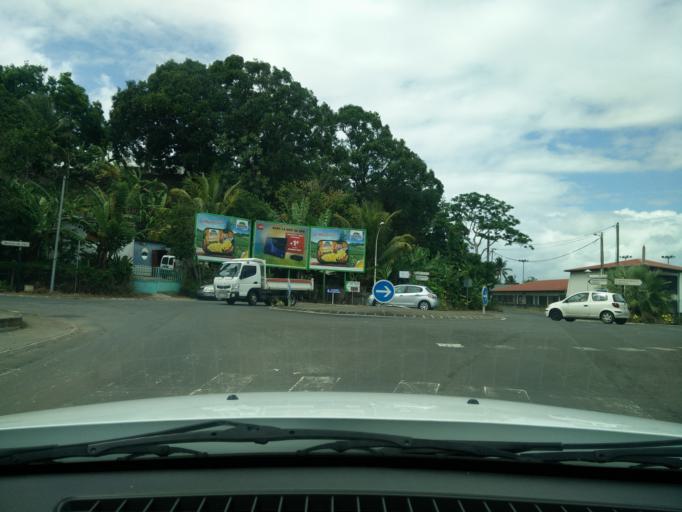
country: GP
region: Guadeloupe
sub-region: Guadeloupe
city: Petit-Bourg
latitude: 16.2045
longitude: -61.6064
